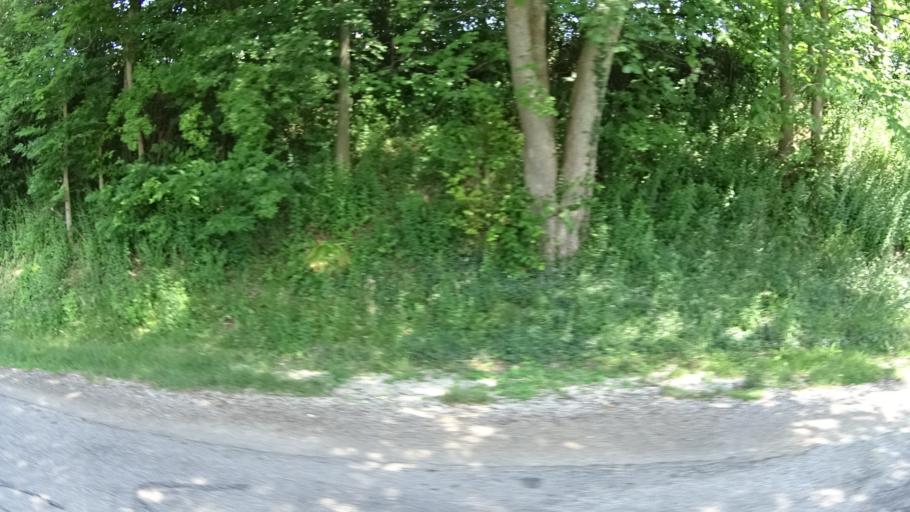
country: US
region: Ohio
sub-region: Lorain County
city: Vermilion
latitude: 41.4250
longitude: -82.3588
